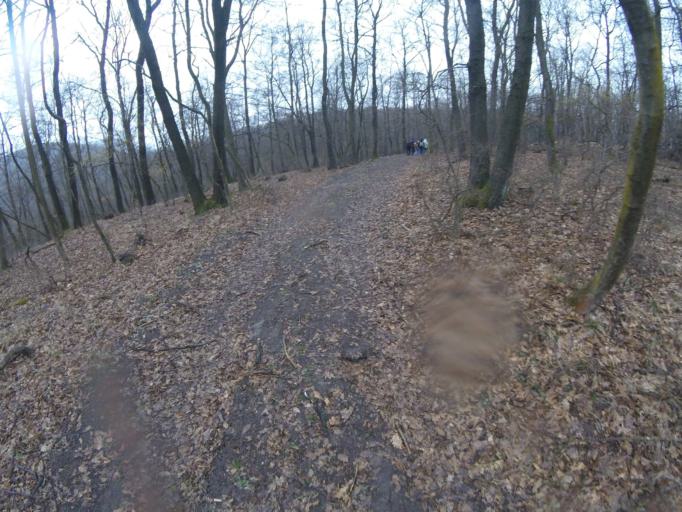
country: HU
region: Pest
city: Szob
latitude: 47.8066
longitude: 18.8246
